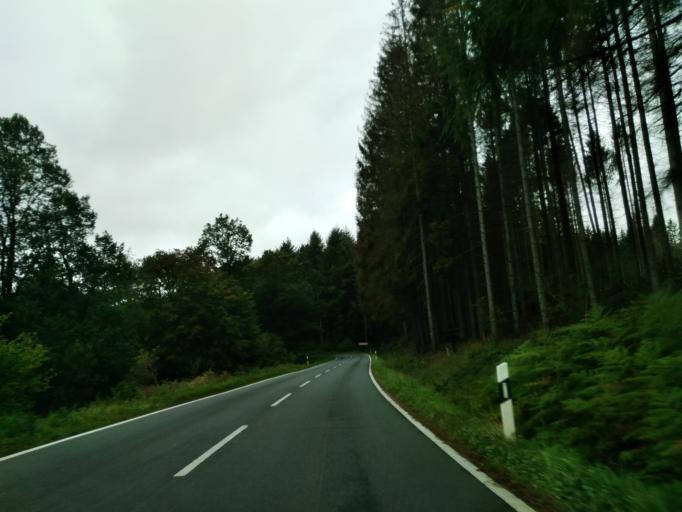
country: DE
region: North Rhine-Westphalia
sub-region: Regierungsbezirk Koln
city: Bad Honnef
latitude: 50.6718
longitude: 7.2863
